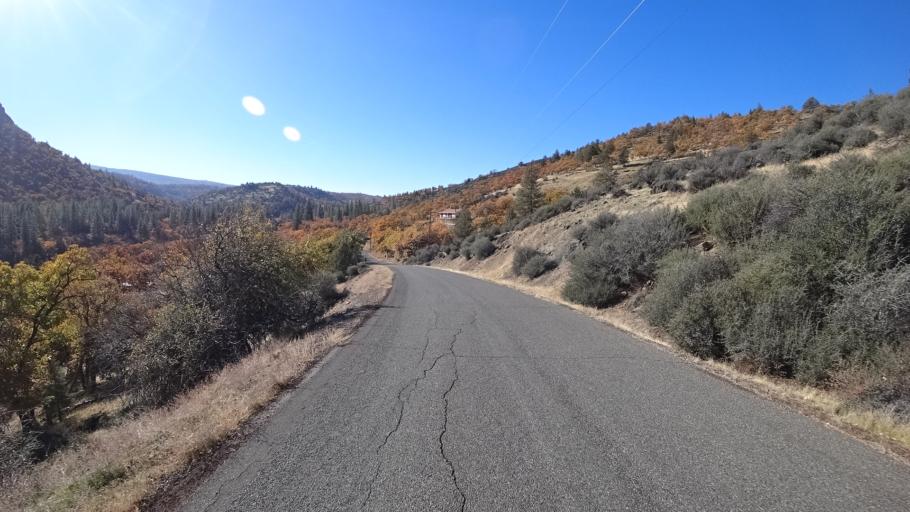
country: US
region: California
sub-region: Siskiyou County
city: Montague
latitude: 41.9752
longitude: -122.3024
